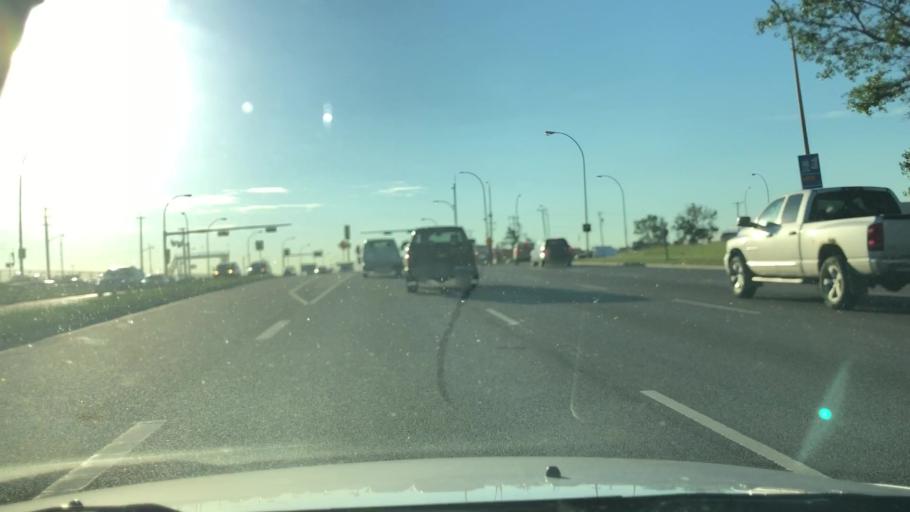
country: CA
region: Alberta
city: Edmonton
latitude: 53.5805
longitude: -113.5276
